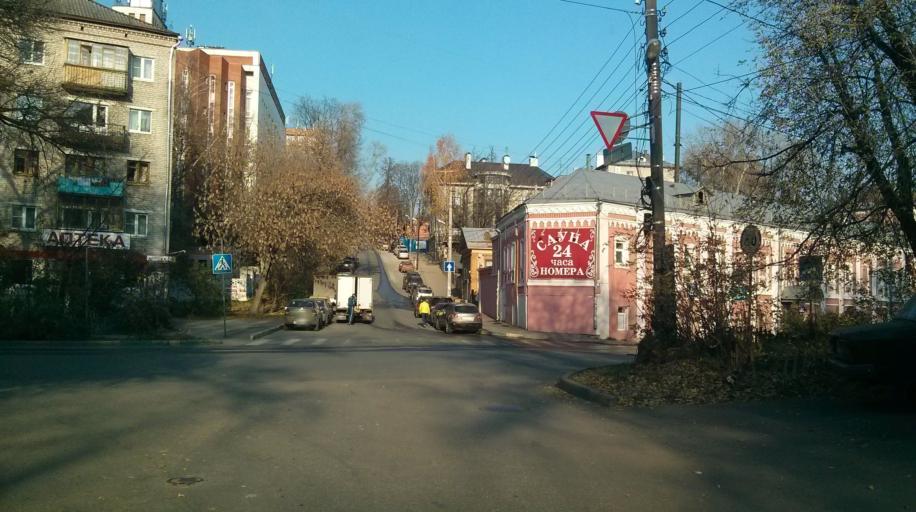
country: RU
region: Nizjnij Novgorod
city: Nizhniy Novgorod
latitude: 56.3211
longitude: 44.0219
